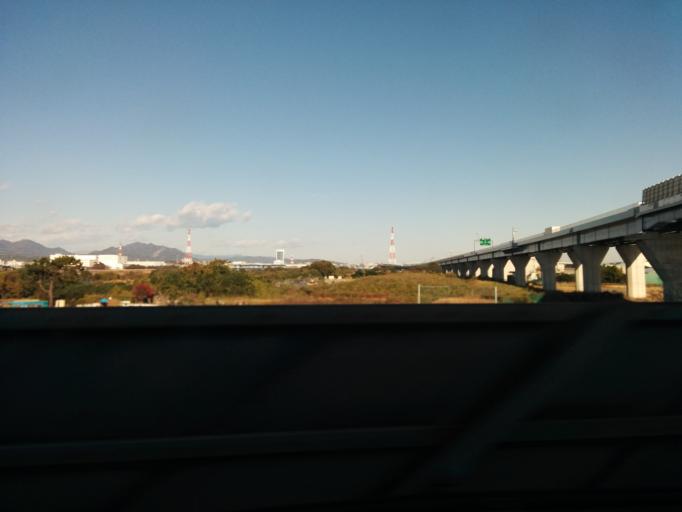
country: JP
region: Kanagawa
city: Atsugi
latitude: 35.3930
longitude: 139.3772
